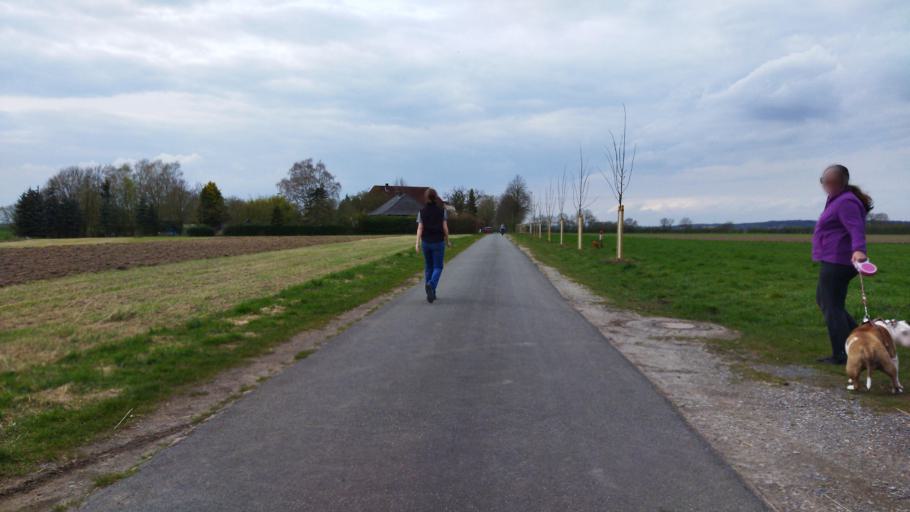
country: DE
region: Lower Saxony
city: Langwedel
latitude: 52.9567
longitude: 9.1911
